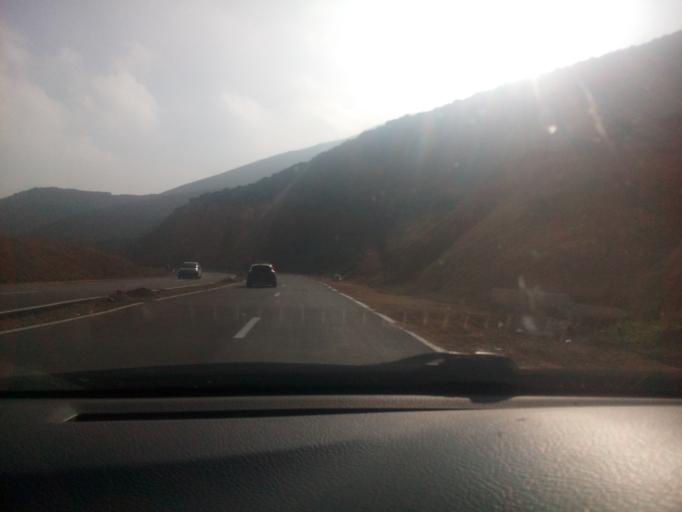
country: DZ
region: Oran
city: Mers el Kebir
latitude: 35.7171
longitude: -0.7100
